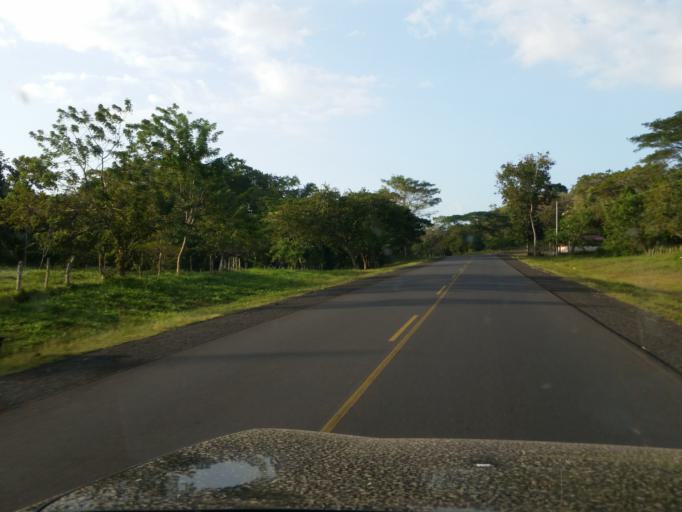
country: NI
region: Rio San Juan
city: San Miguelito
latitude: 11.3708
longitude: -84.7749
